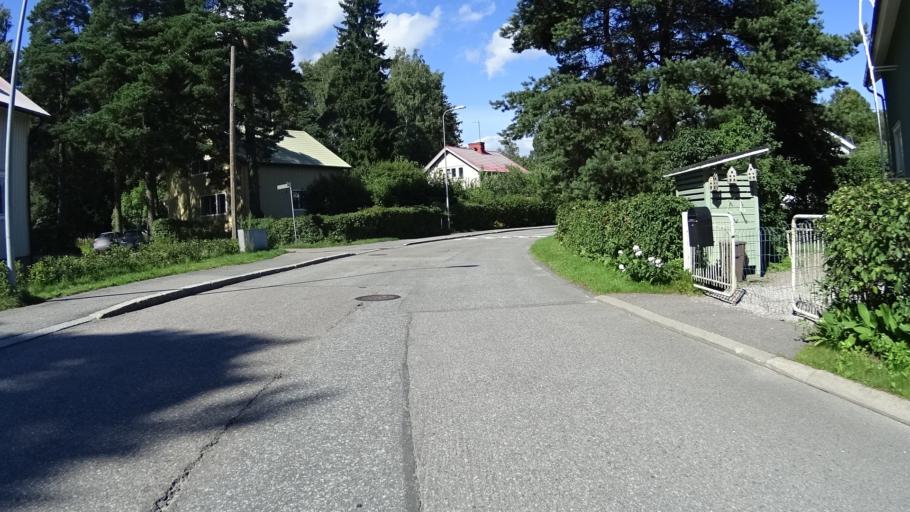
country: FI
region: Uusimaa
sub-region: Helsinki
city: Teekkarikylae
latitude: 60.2263
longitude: 24.8632
